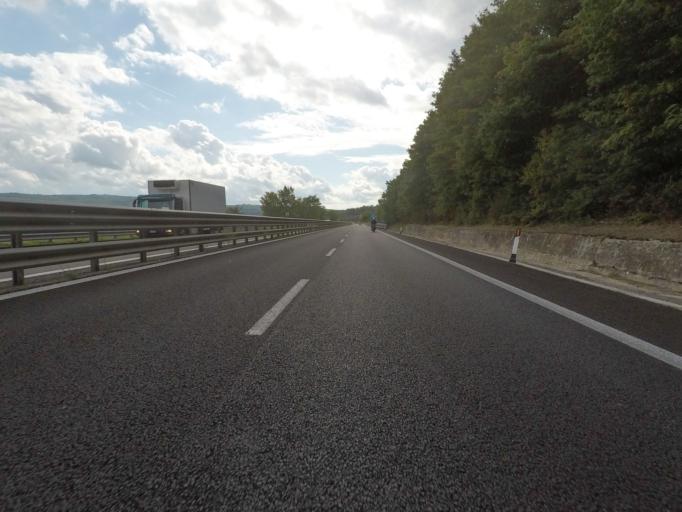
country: IT
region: Tuscany
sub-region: Provincia di Siena
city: Serre di Rapolano
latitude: 43.2608
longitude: 11.6310
